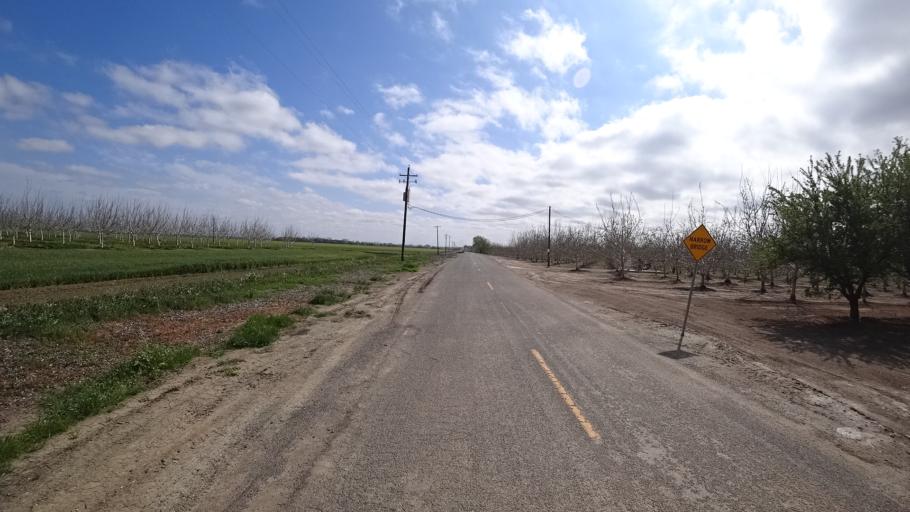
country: US
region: California
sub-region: Colusa County
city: Colusa
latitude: 39.4200
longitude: -121.9433
